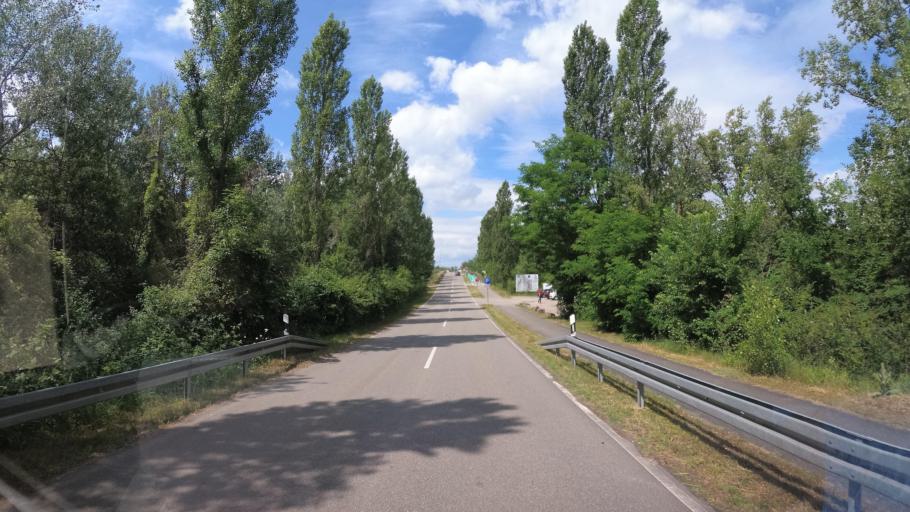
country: FR
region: Alsace
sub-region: Departement du Haut-Rhin
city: Fessenheim
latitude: 47.9084
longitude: 7.5864
